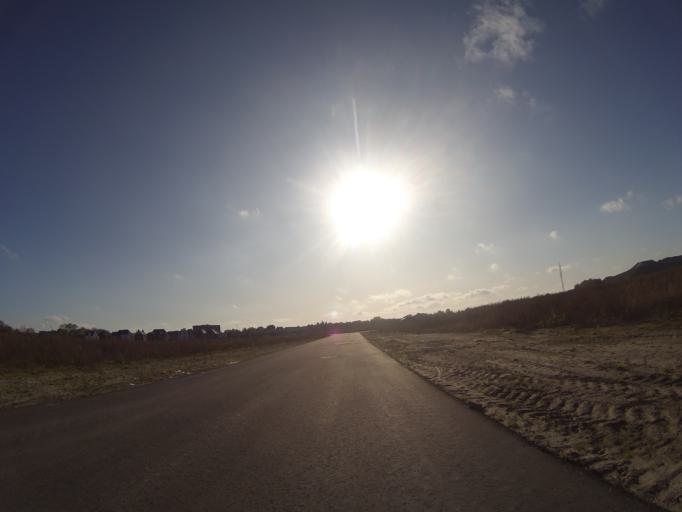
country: NL
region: Utrecht
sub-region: Gemeente Amersfoort
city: Hoogland
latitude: 52.2065
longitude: 5.4119
